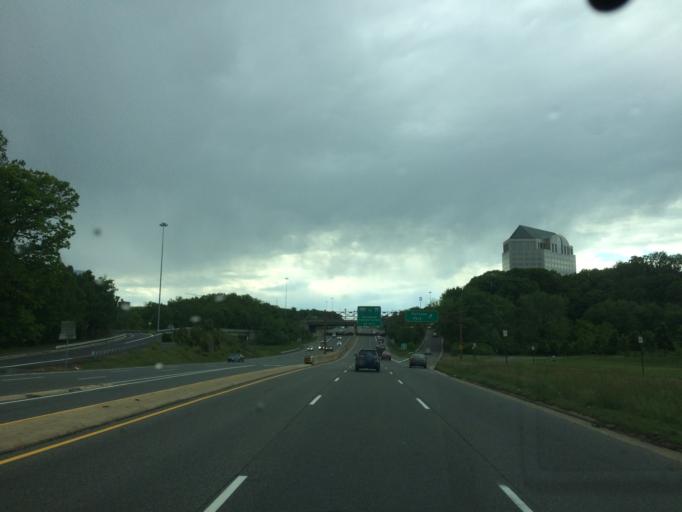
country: US
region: Virginia
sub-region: Fairfax County
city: Merrifield
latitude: 38.8660
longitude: -77.2095
